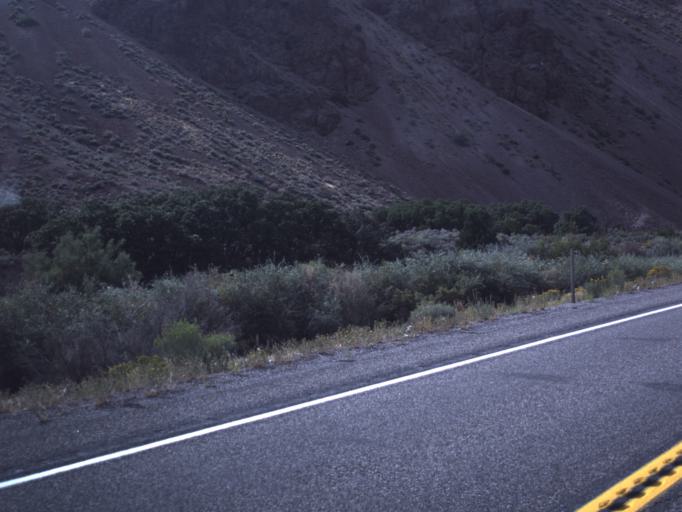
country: US
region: Utah
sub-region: Sevier County
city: Monroe
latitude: 38.4972
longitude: -112.2560
